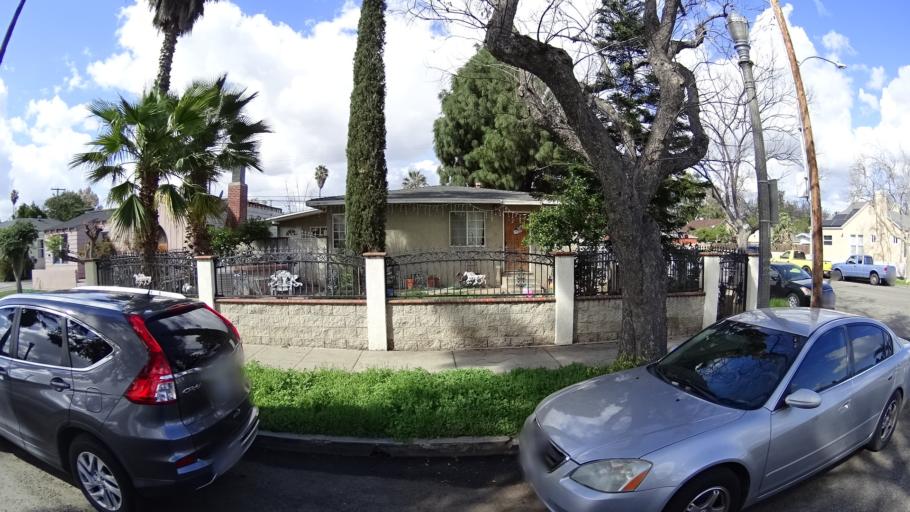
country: US
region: California
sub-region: Orange County
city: Anaheim
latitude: 33.8454
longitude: -117.9112
